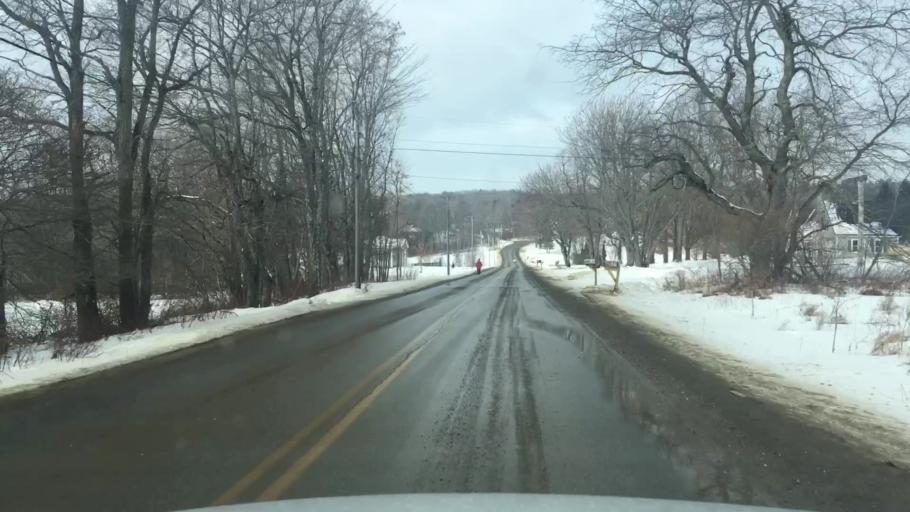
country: US
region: Maine
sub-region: Penobscot County
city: Hermon
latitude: 44.7658
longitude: -68.9557
